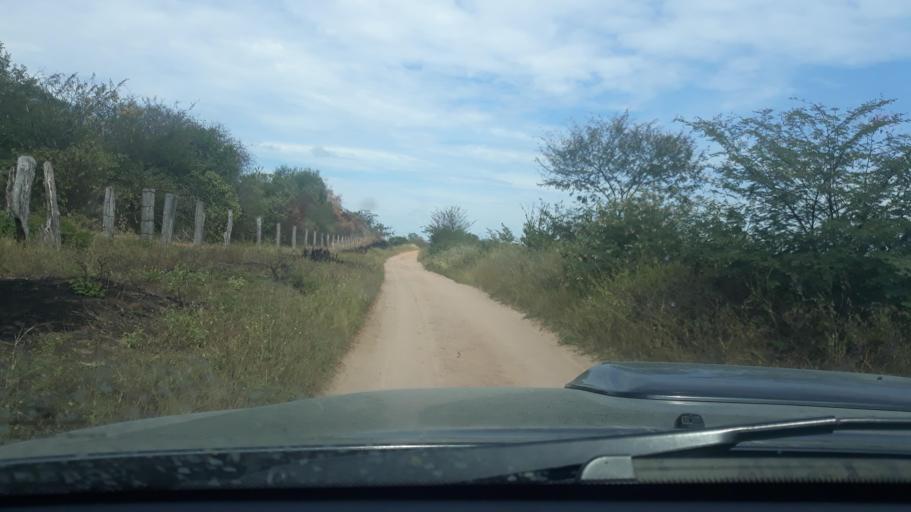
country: BR
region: Bahia
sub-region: Riacho De Santana
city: Riacho de Santana
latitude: -13.8546
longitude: -43.0576
